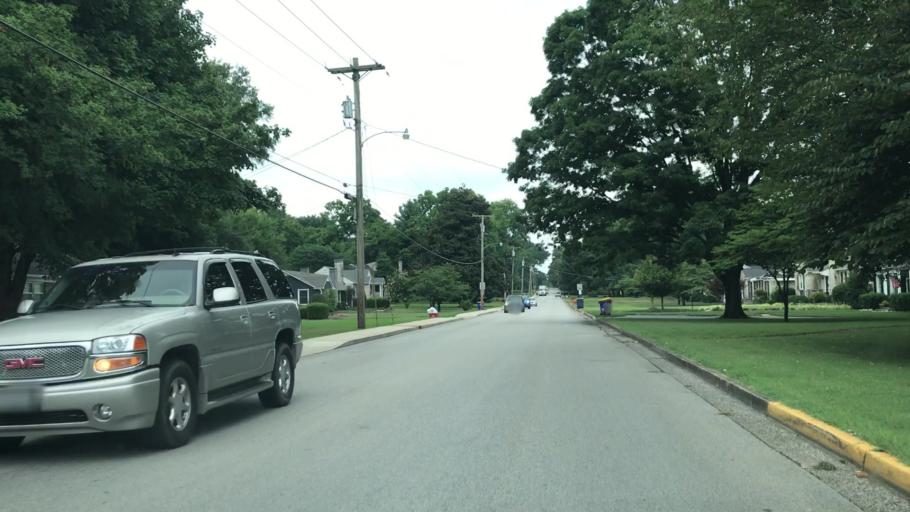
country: US
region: Kentucky
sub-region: Warren County
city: Bowling Green
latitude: 36.9824
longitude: -86.4277
